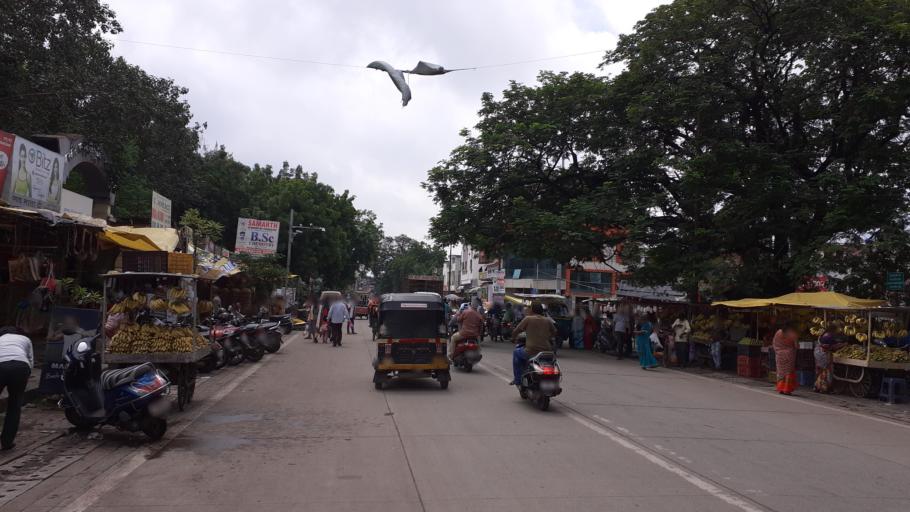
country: IN
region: Maharashtra
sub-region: Nagpur Division
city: Nagpur
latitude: 21.1275
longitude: 79.1131
